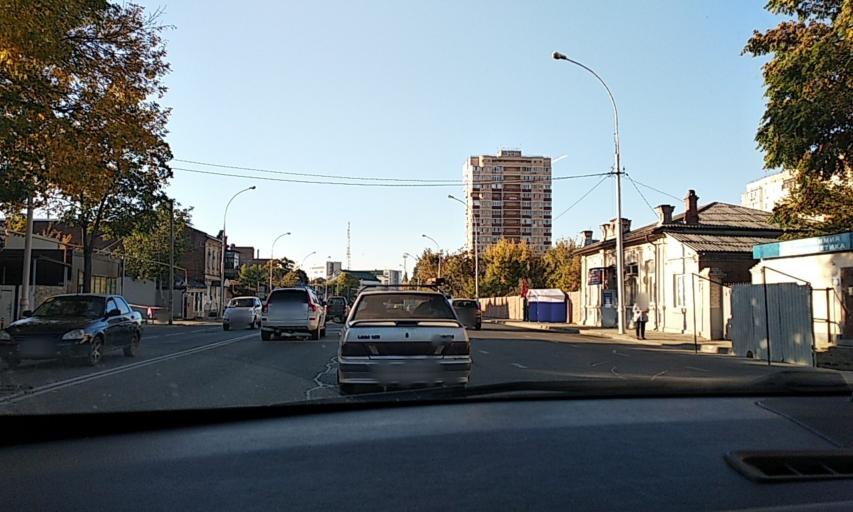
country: RU
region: Krasnodarskiy
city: Krasnodar
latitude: 45.0186
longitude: 38.9806
